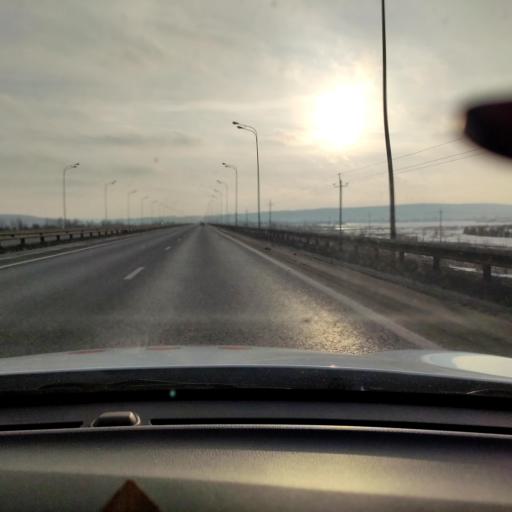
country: RU
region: Tatarstan
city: Osinovo
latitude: 55.8112
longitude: 48.8415
